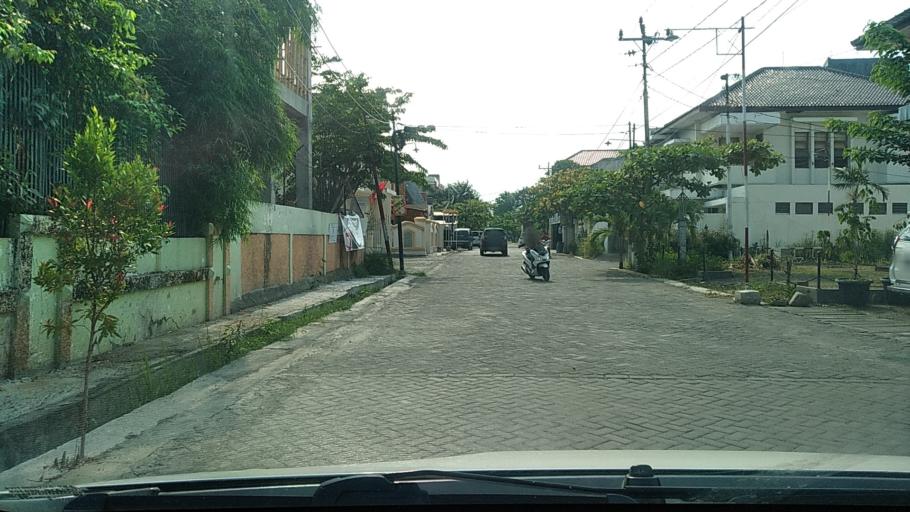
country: ID
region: Central Java
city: Semarang
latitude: -6.9692
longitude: 110.3982
